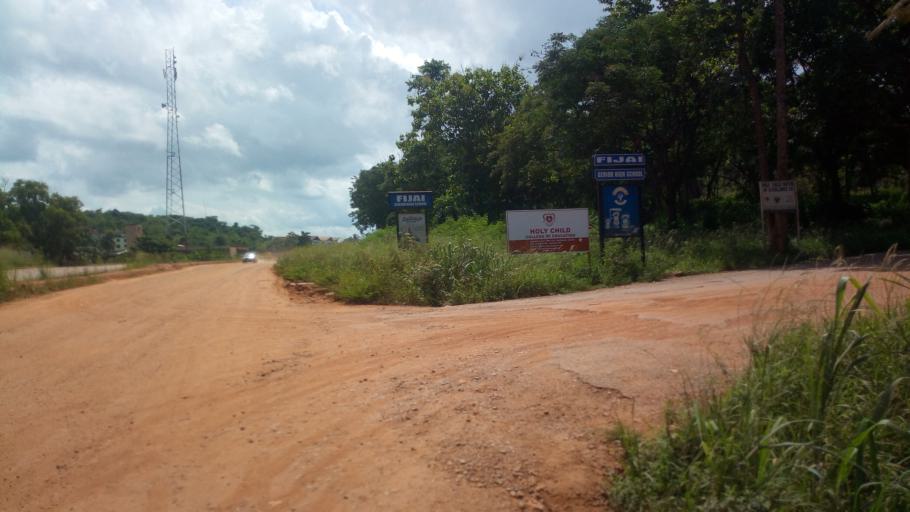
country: GH
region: Western
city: Sekondi-Takoradi
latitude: 4.9279
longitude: -1.7461
